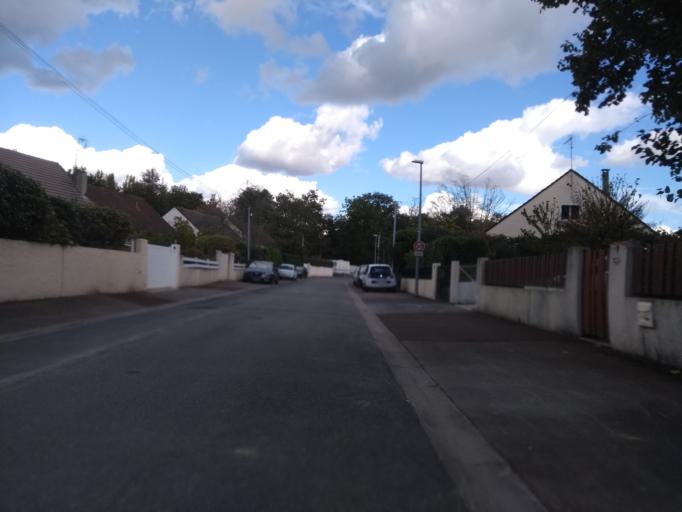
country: FR
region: Aquitaine
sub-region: Departement de la Gironde
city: Canejan
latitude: 44.7599
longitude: -0.6384
